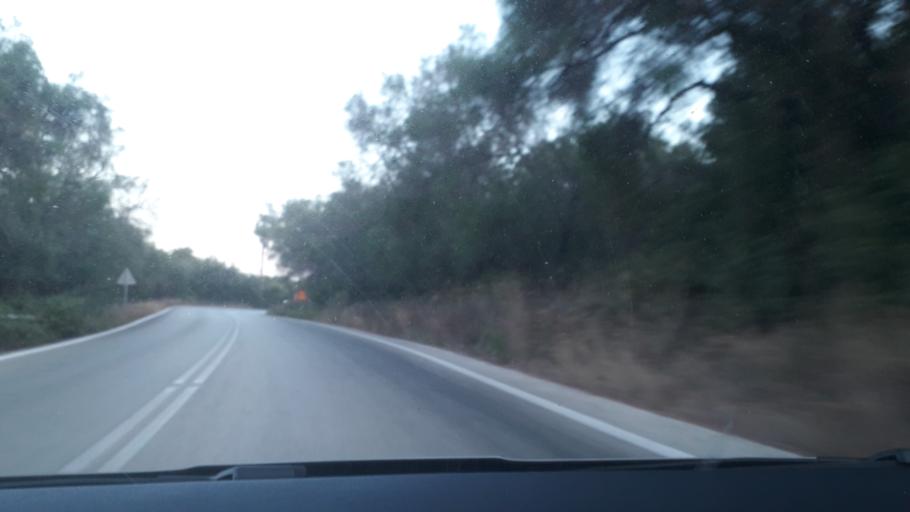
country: GR
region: Ionian Islands
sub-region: Nomos Kerkyras
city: Agios Matthaios
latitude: 39.4491
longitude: 19.9295
